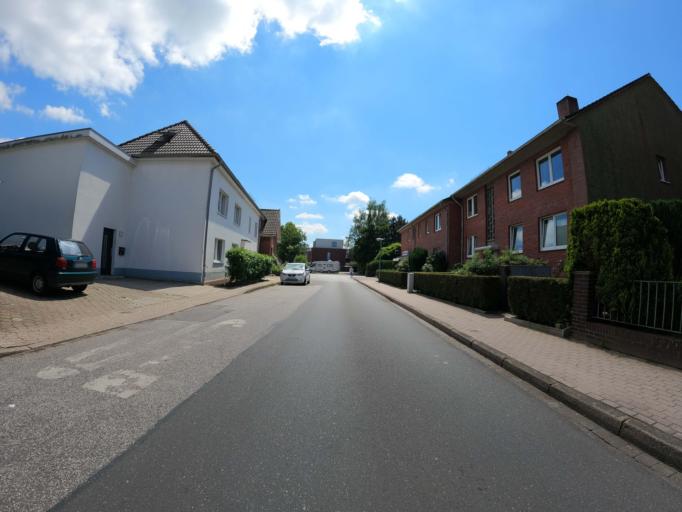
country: DE
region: Schleswig-Holstein
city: Wentorf bei Hamburg
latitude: 53.4923
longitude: 10.2563
